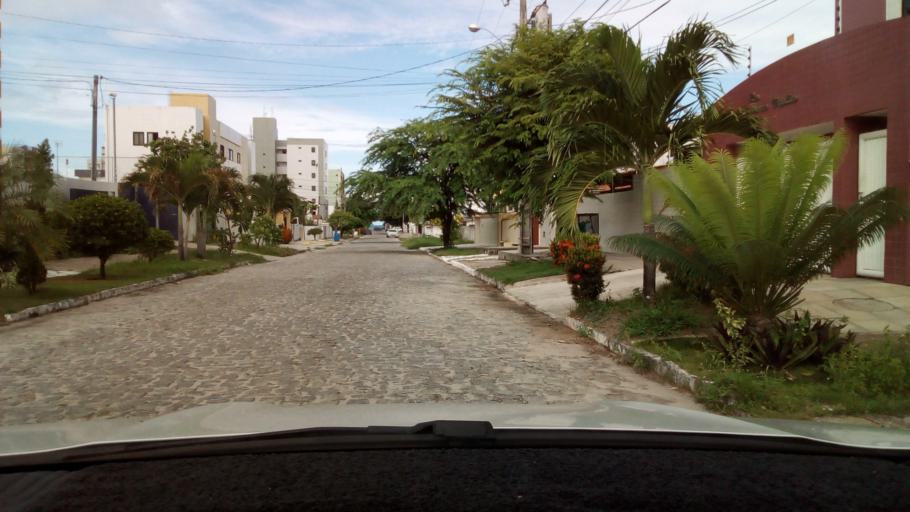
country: BR
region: Paraiba
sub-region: Joao Pessoa
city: Joao Pessoa
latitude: -7.0670
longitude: -34.8427
